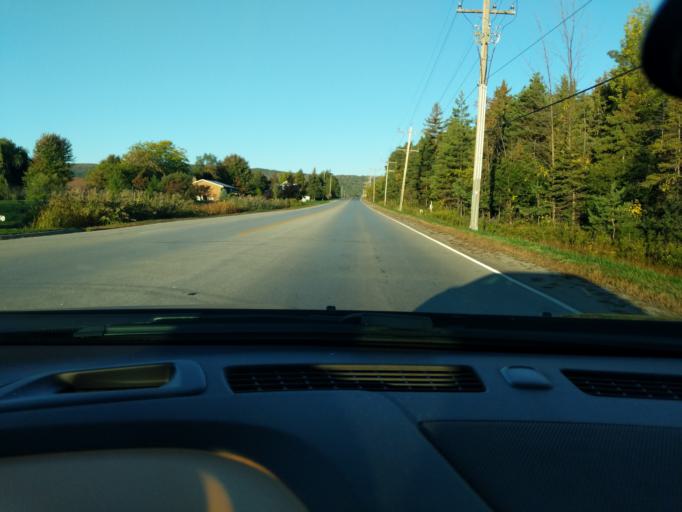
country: CA
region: Ontario
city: Collingwood
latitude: 44.4986
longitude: -80.2628
